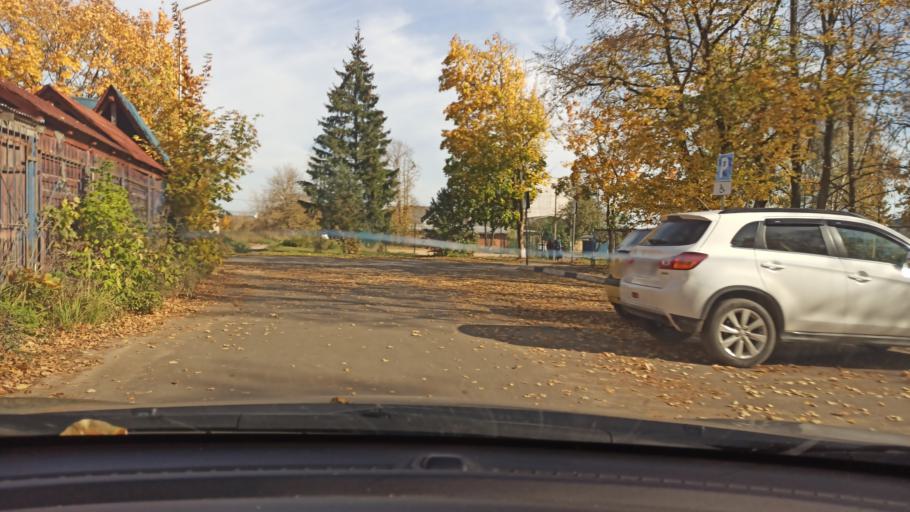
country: RU
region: Moskovskaya
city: Kurovskoye
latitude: 55.5820
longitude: 38.9385
